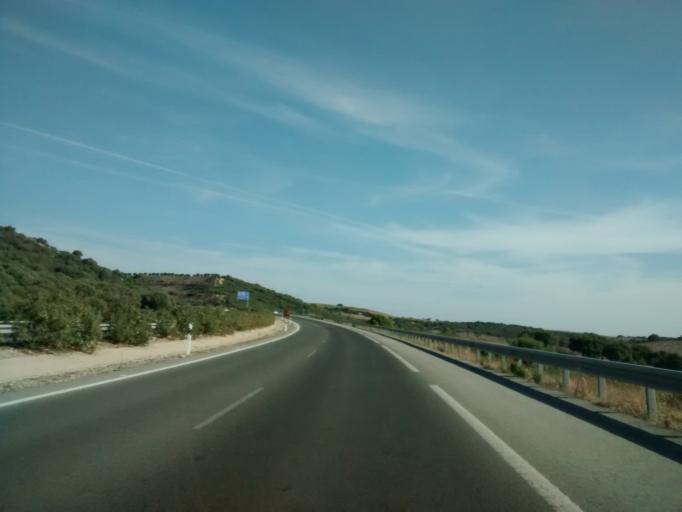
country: ES
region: Andalusia
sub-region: Provincia de Cadiz
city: Conil de la Frontera
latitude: 36.3364
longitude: -6.0489
